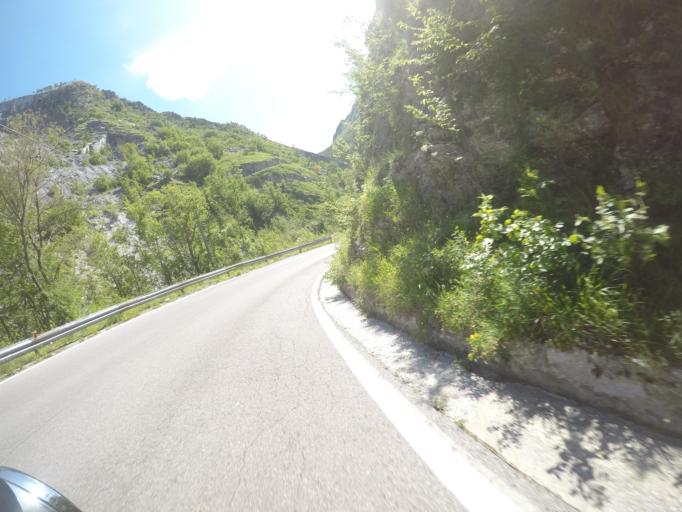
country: IT
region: Tuscany
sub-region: Provincia di Lucca
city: Fontana delle Monache
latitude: 44.0580
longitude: 10.2638
